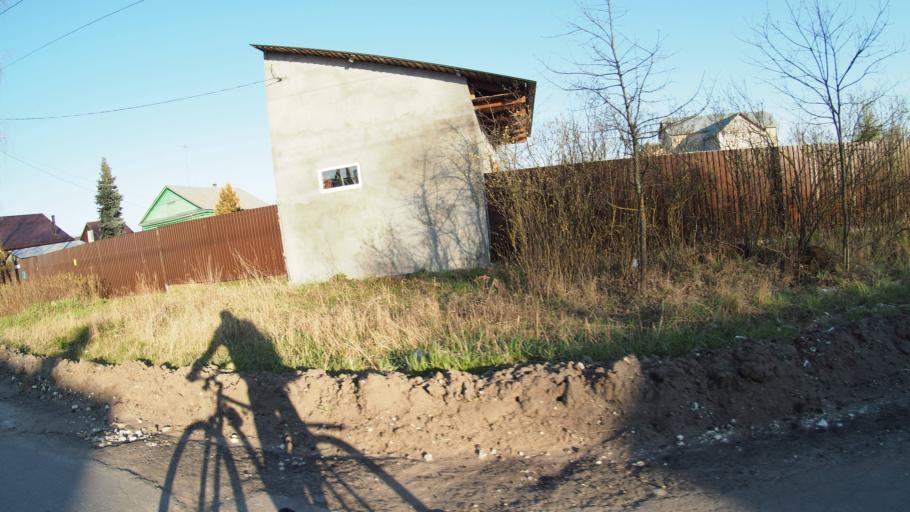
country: RU
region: Moskovskaya
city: Malyshevo
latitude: 55.4924
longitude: 38.3488
